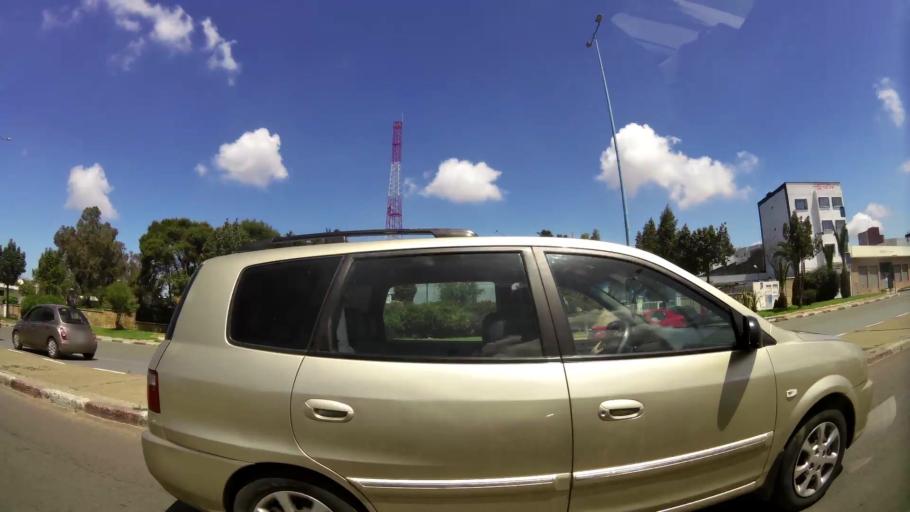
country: MA
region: Grand Casablanca
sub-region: Casablanca
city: Casablanca
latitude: 33.5494
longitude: -7.5869
